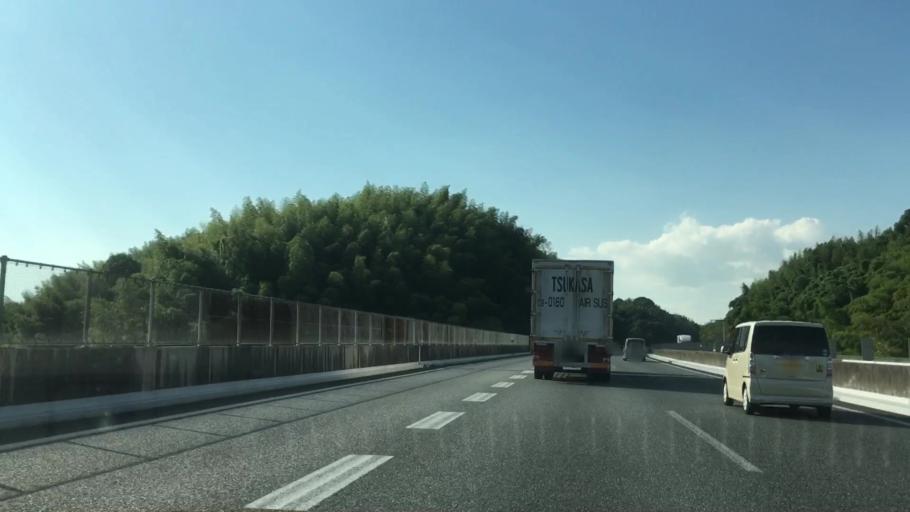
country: JP
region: Yamaguchi
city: Kudamatsu
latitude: 34.0317
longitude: 131.9349
